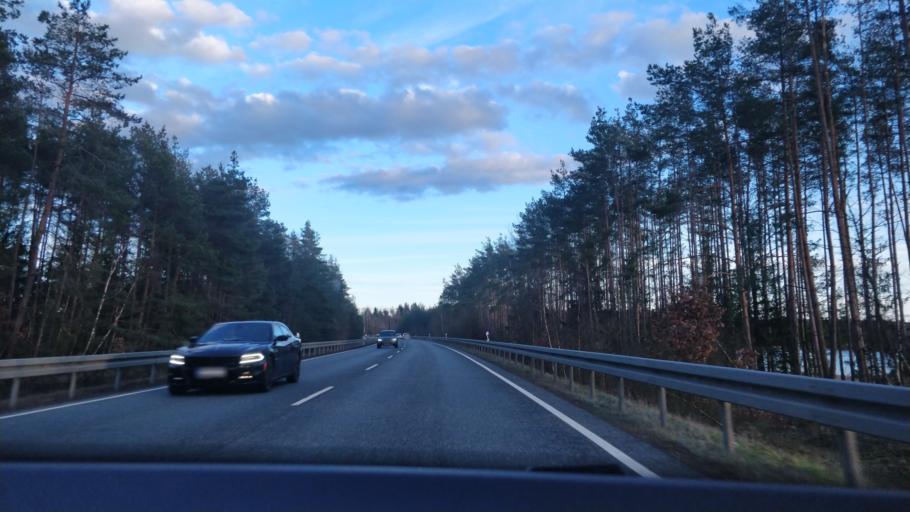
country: DE
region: Bavaria
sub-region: Upper Palatinate
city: Schwarzenbach
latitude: 49.7231
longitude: 11.9716
